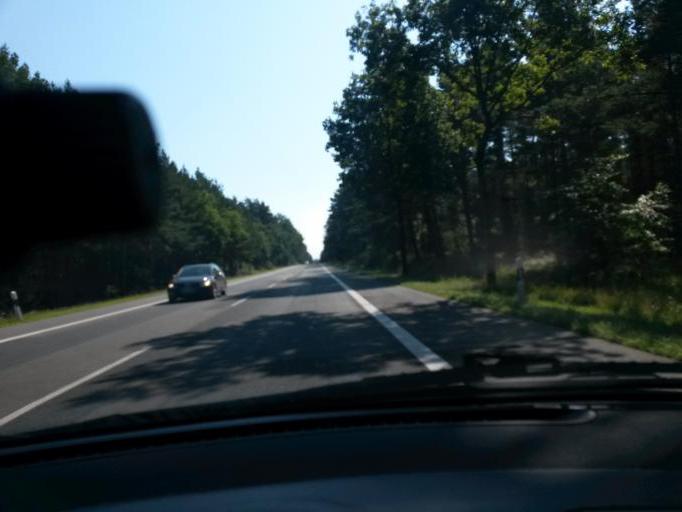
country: DE
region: Lower Saxony
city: Barendorf
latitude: 53.2333
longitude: 10.4960
